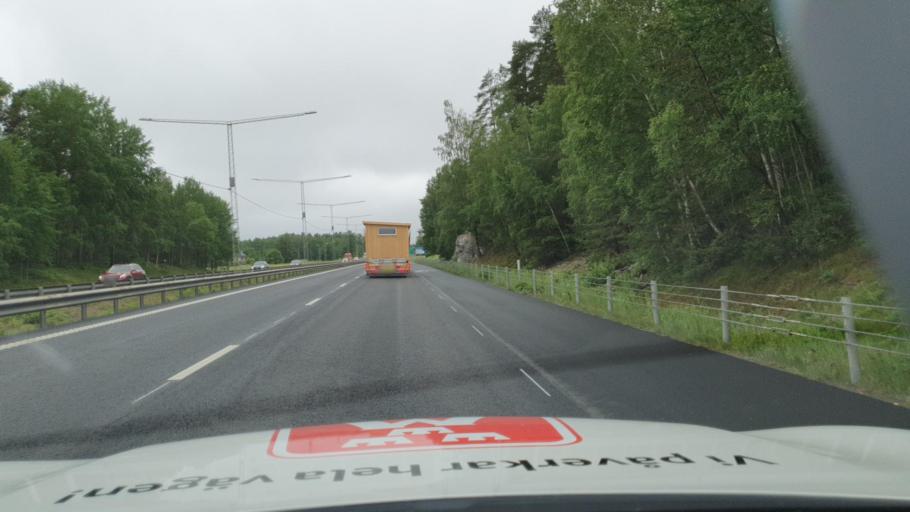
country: SE
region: Vaermland
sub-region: Karlstads Kommun
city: Karlstad
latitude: 59.3810
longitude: 13.4533
